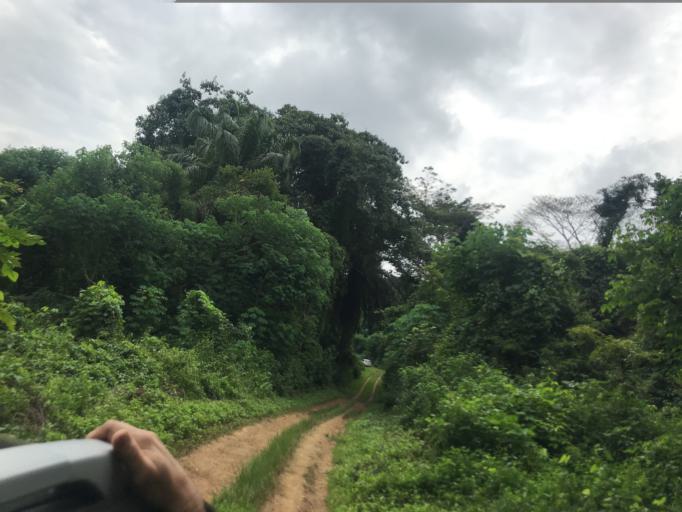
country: AO
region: Cuanza Norte
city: N'dalatando
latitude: -9.0740
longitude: 14.8076
